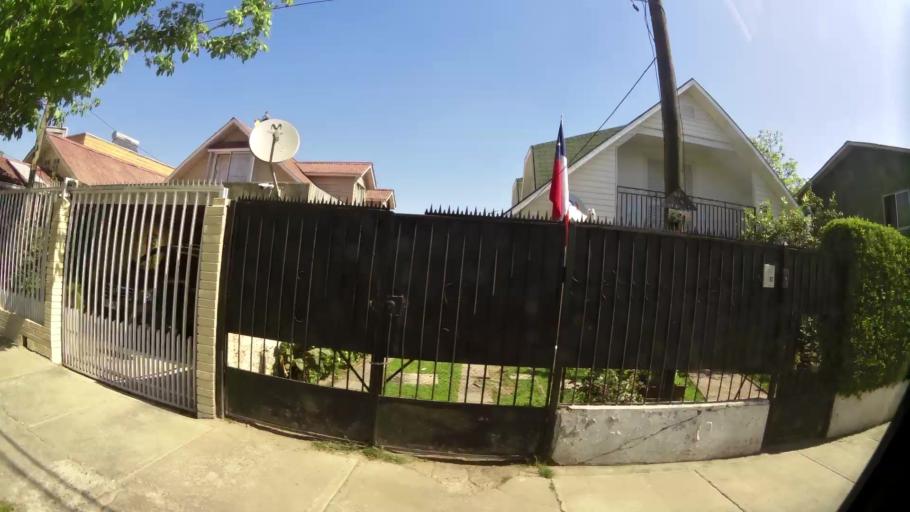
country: CL
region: Santiago Metropolitan
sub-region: Provincia de Talagante
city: Penaflor
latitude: -33.5674
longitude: -70.8062
